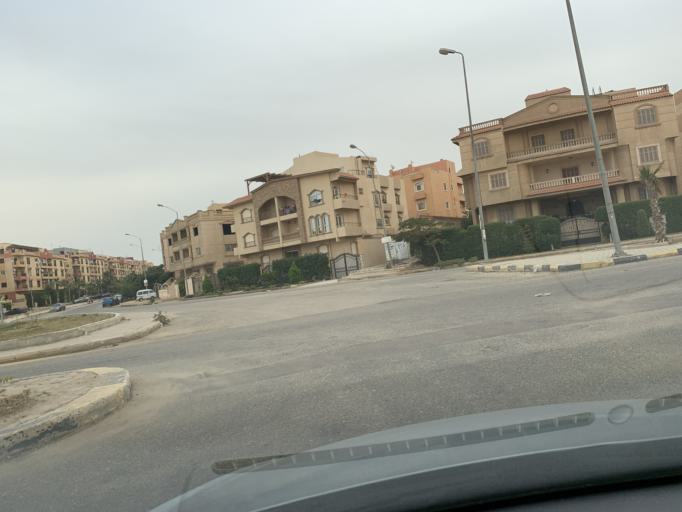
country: EG
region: Al Jizah
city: Awsim
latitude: 30.0310
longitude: 30.9799
